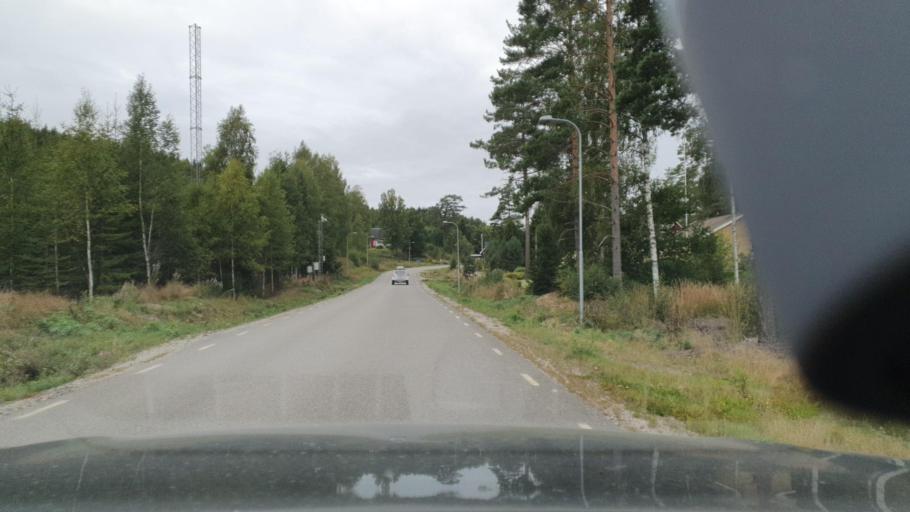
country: SE
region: Vaermland
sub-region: Eda Kommun
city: Charlottenberg
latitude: 60.0198
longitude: 12.6241
